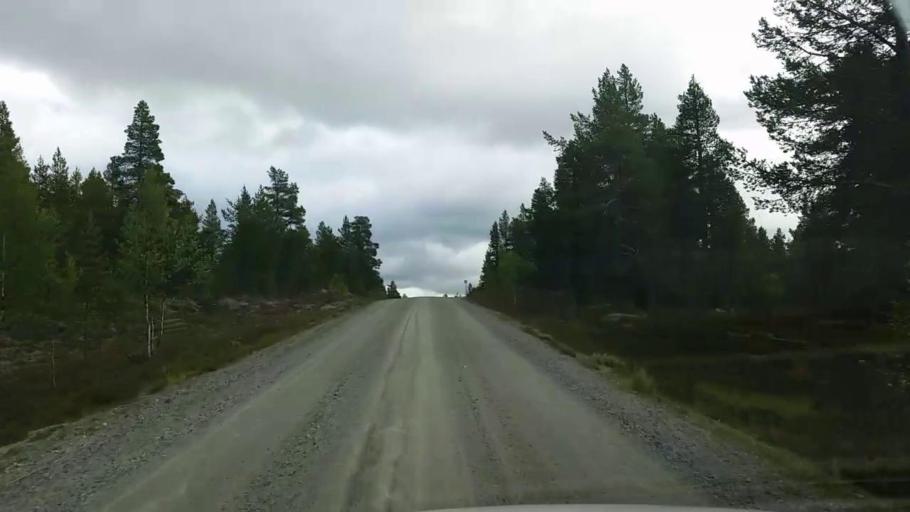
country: NO
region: Hedmark
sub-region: Engerdal
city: Engerdal
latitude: 62.3412
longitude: 12.6110
